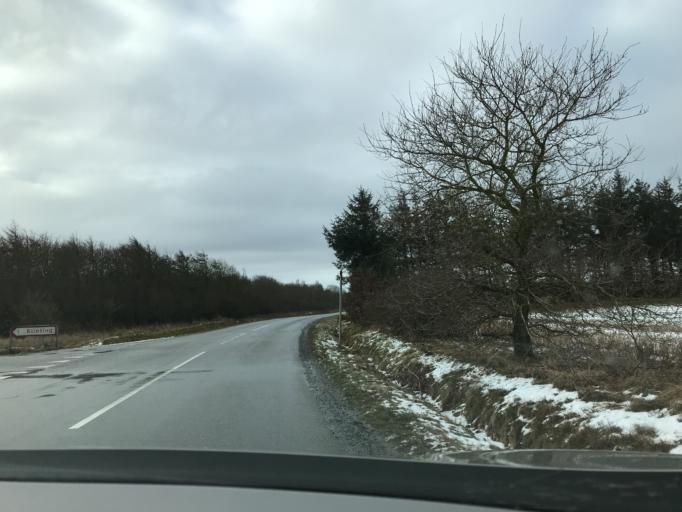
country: DK
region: South Denmark
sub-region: Varde Kommune
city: Oksbol
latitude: 55.7685
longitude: 8.2682
